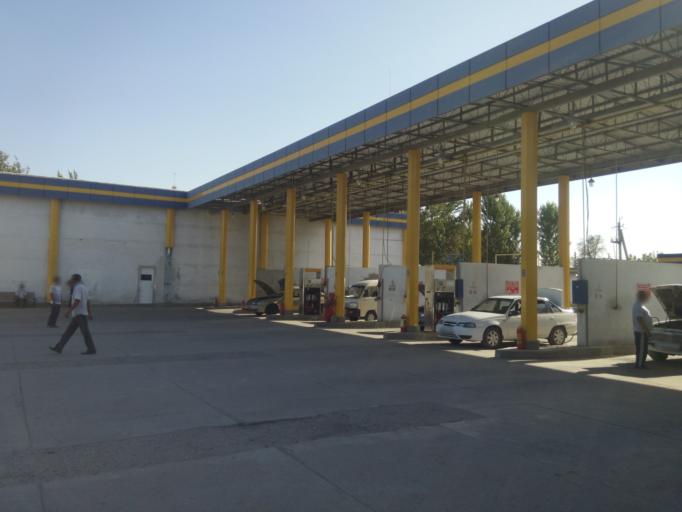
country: UZ
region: Sirdaryo
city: Guliston
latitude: 40.5077
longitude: 68.7630
